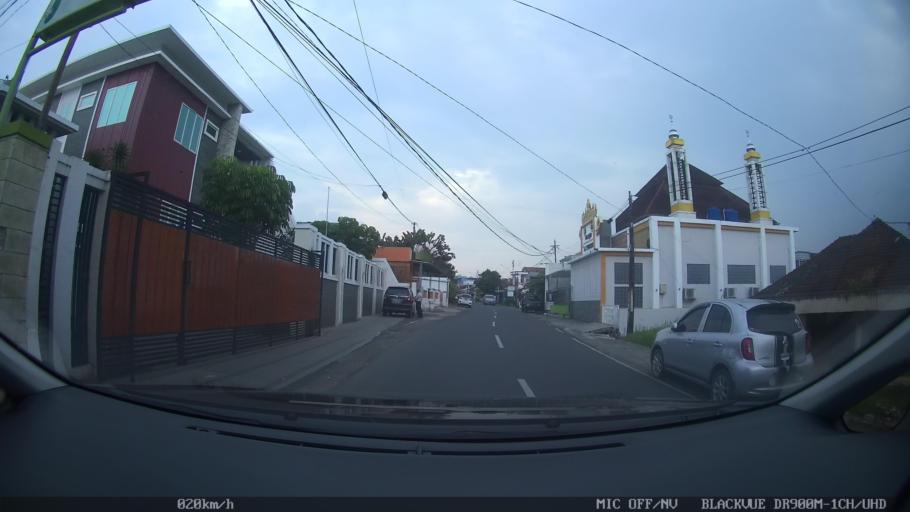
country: ID
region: Lampung
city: Bandarlampung
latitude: -5.4249
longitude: 105.2562
